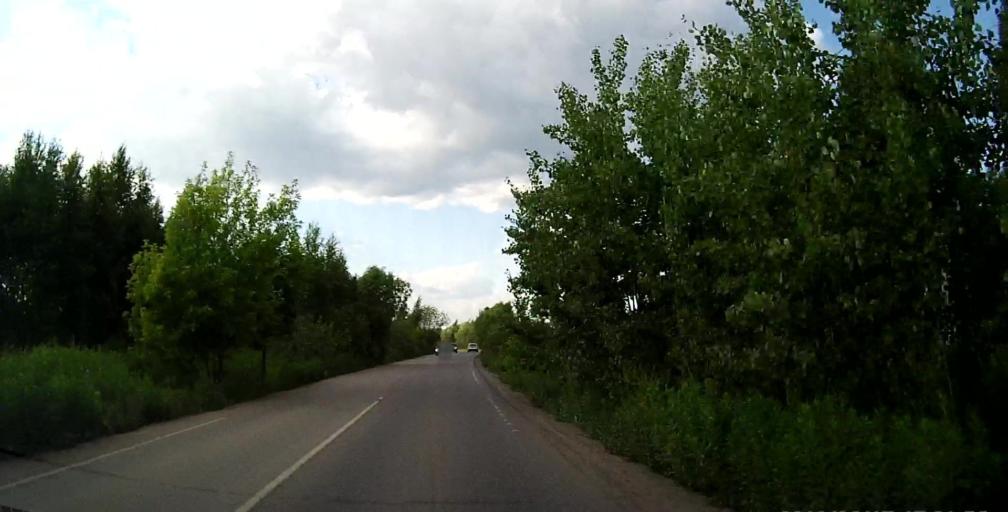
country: RU
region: Moskovskaya
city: Shcherbinka
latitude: 55.5199
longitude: 37.5345
